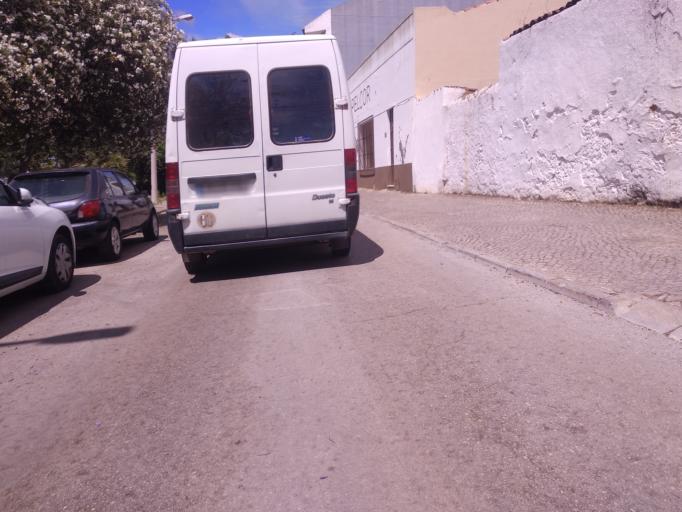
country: PT
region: Faro
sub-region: Sao Bras de Alportel
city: Sao Bras de Alportel
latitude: 37.1540
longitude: -7.8864
